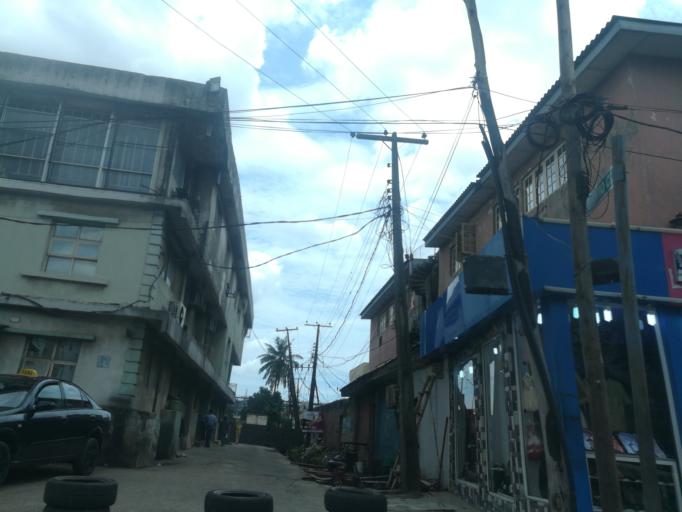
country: NG
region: Lagos
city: Ikeja
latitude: 6.5961
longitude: 3.3509
